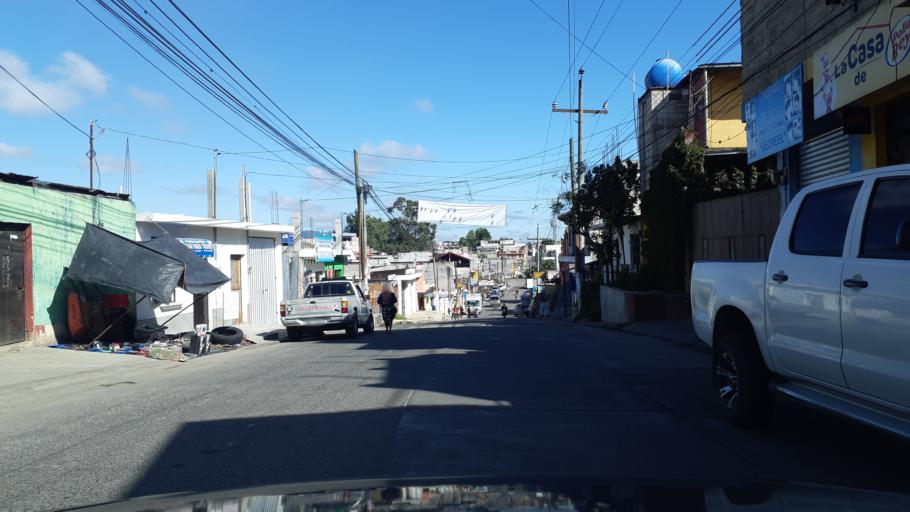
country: GT
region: Chimaltenango
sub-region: Municipio de Chimaltenango
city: Chimaltenango
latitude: 14.6569
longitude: -90.8220
